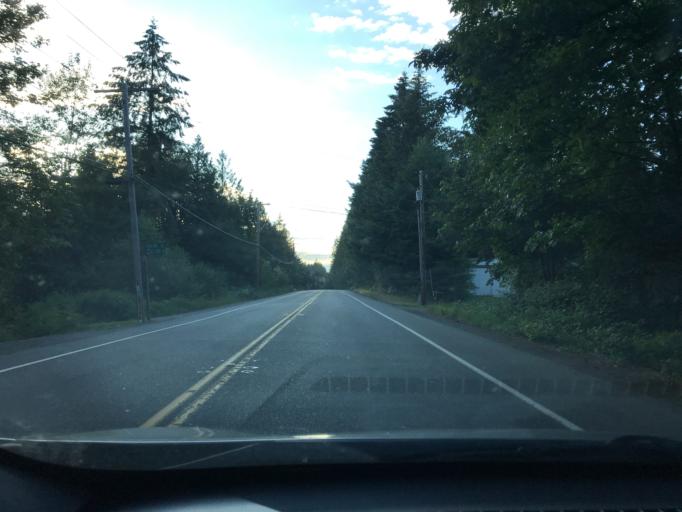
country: US
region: Washington
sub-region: King County
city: Lake Morton-Berrydale
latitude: 47.3101
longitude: -122.0918
